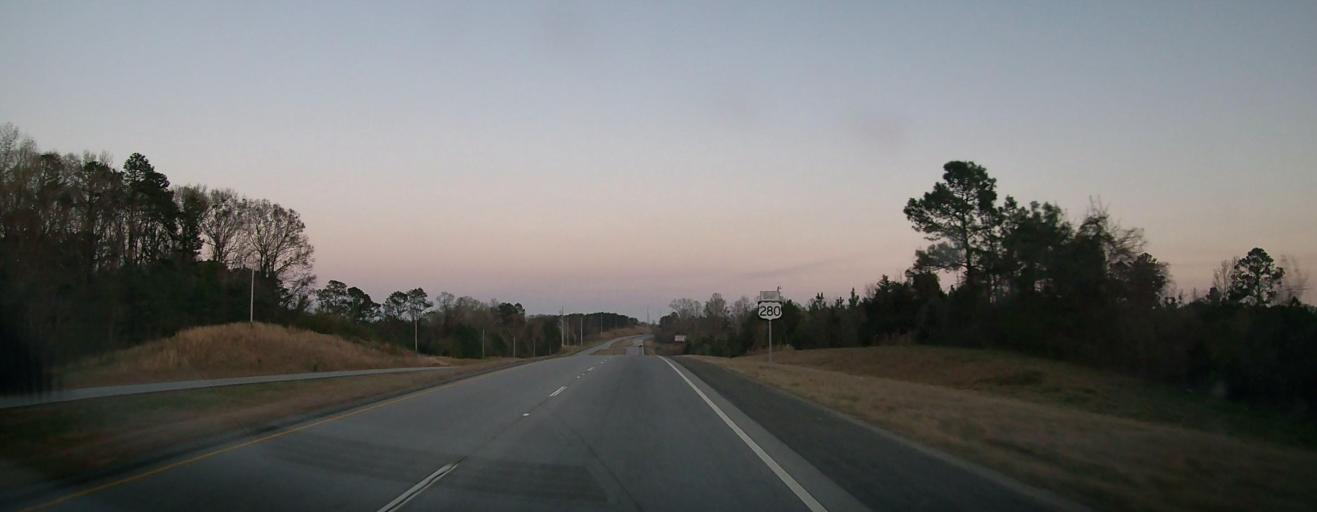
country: US
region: Alabama
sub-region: Tallapoosa County
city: Dadeville
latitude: 32.8617
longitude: -85.7953
